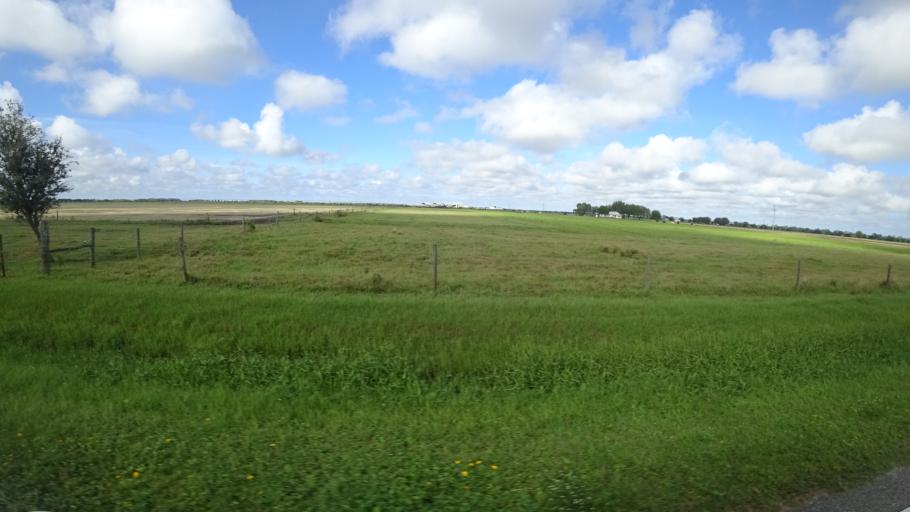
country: US
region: Florida
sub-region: Sarasota County
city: Lake Sarasota
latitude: 27.3688
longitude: -82.2684
